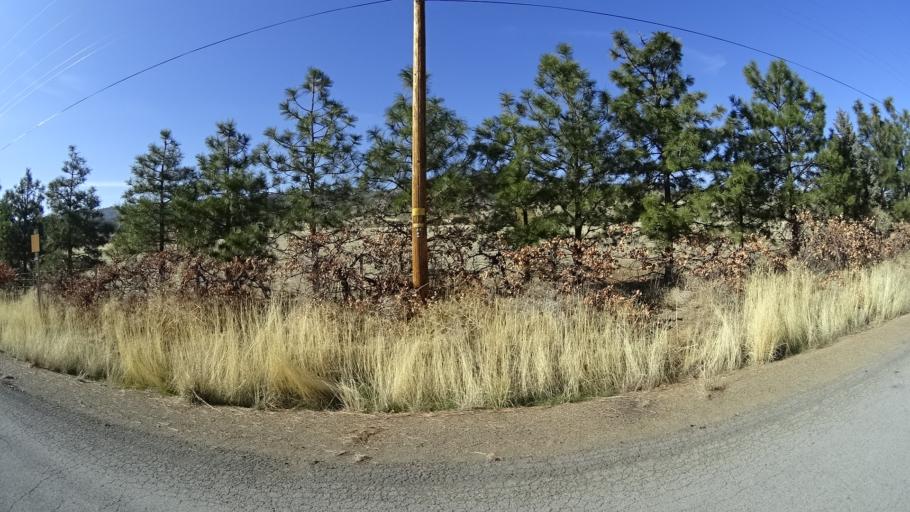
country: US
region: California
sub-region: Siskiyou County
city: Montague
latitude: 41.5945
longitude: -122.5409
